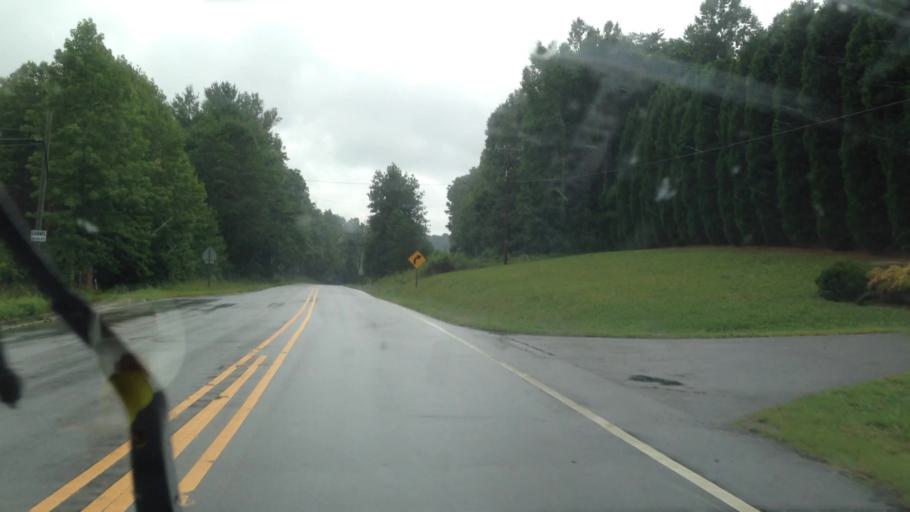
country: US
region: North Carolina
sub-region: Rockingham County
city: Mayodan
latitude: 36.4045
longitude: -79.9801
